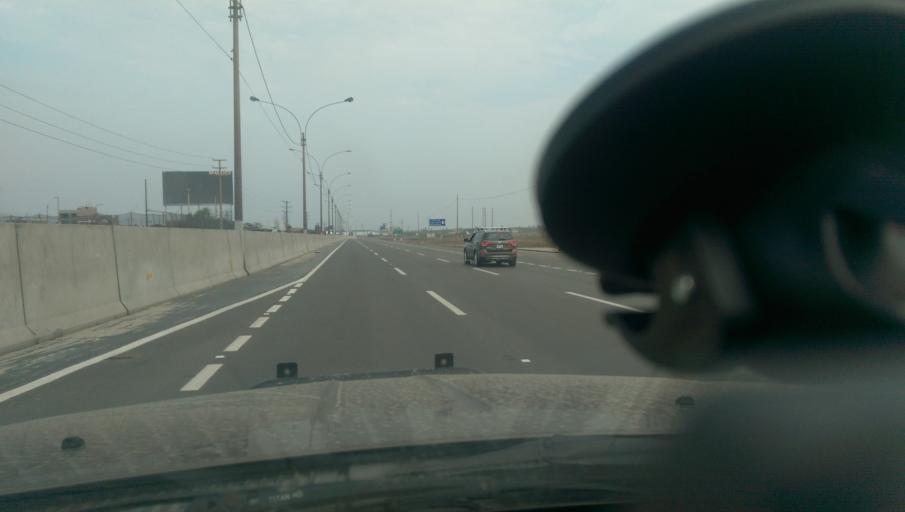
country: PE
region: Lima
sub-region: Lima
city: Santa Rosa
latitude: -11.7839
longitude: -77.1555
